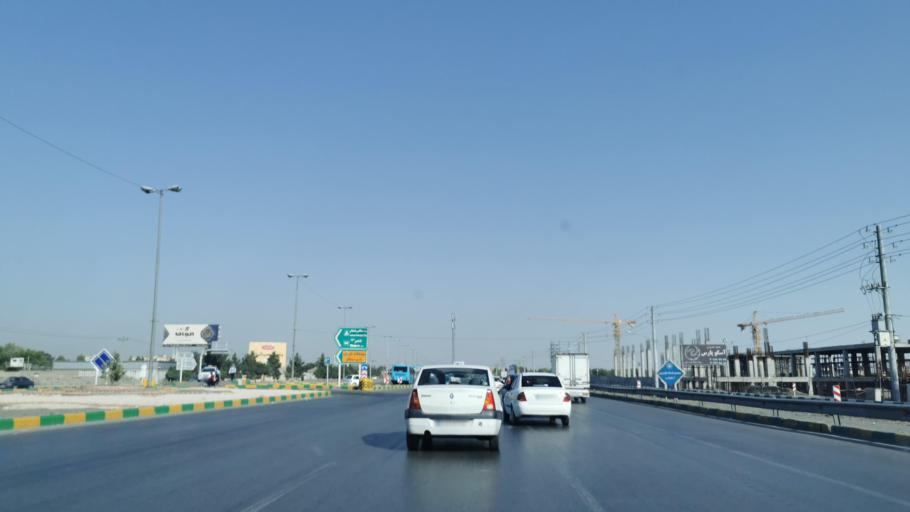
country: IR
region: Razavi Khorasan
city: Mashhad
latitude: 36.3959
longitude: 59.4961
